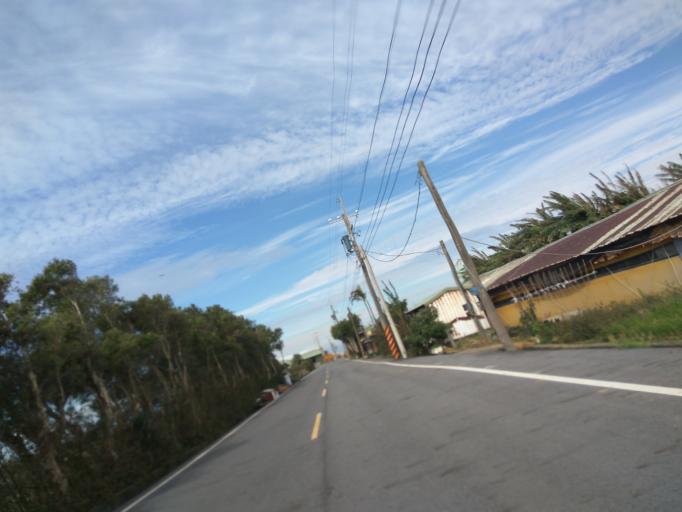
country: TW
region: Taiwan
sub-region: Hsinchu
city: Zhubei
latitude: 25.0046
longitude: 121.0812
